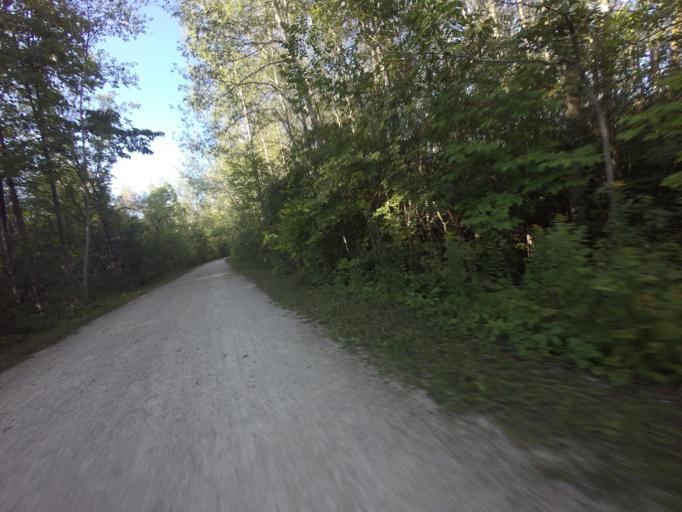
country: CA
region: Ontario
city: Orangeville
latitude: 43.8087
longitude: -79.9326
